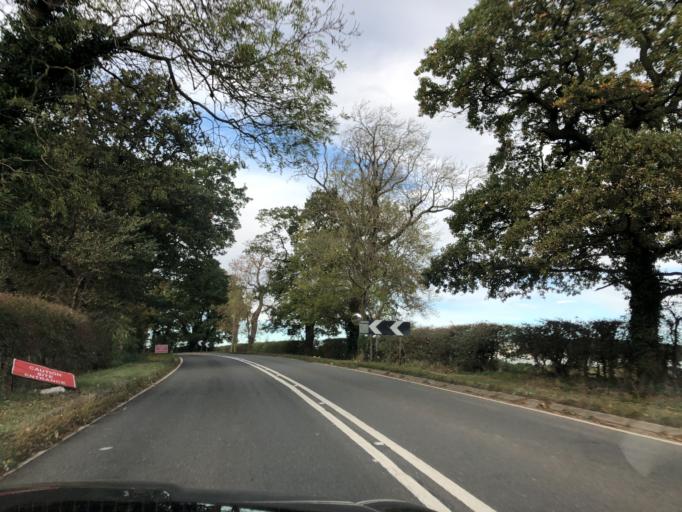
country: GB
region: England
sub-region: Warwickshire
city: Warwick
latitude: 52.2508
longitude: -1.5590
